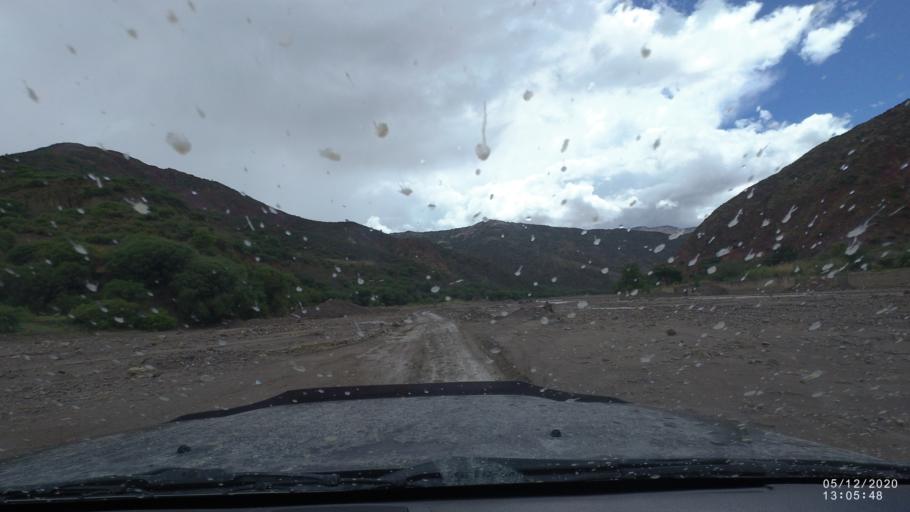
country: BO
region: Cochabamba
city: Sipe Sipe
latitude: -17.5560
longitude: -66.4429
